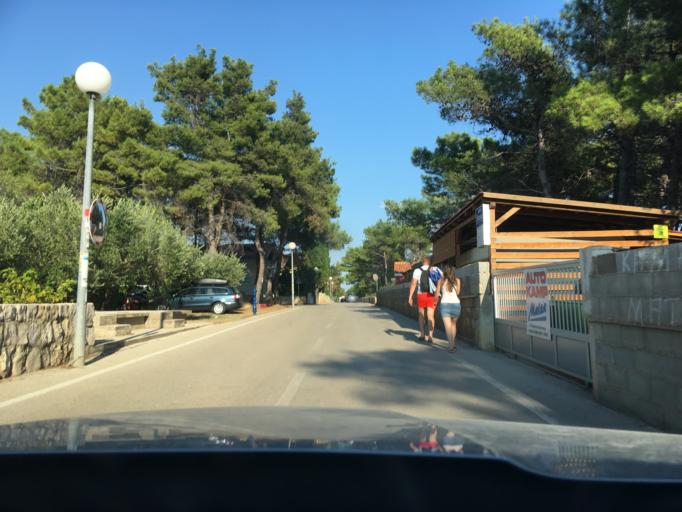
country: HR
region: Zadarska
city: Vir
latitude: 44.2979
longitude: 15.0973
